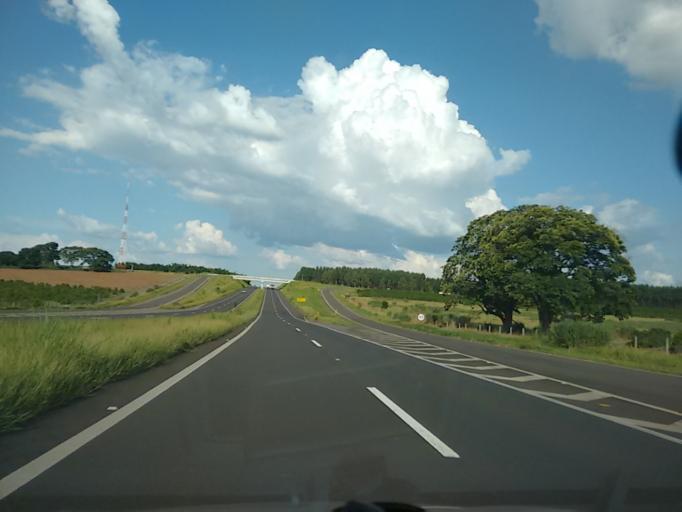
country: BR
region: Sao Paulo
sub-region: Duartina
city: Duartina
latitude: -22.3306
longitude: -49.4554
